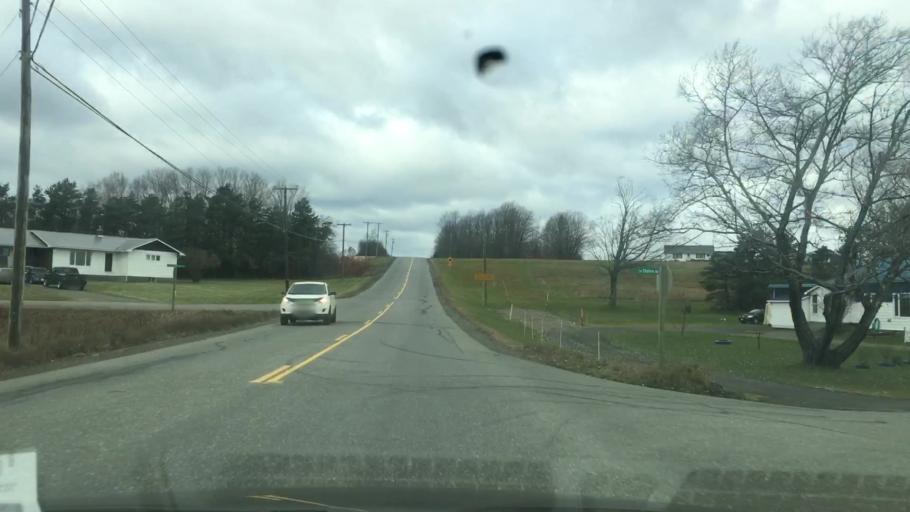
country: US
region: Maine
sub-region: Aroostook County
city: Fort Fairfield
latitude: 46.7595
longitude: -67.7718
